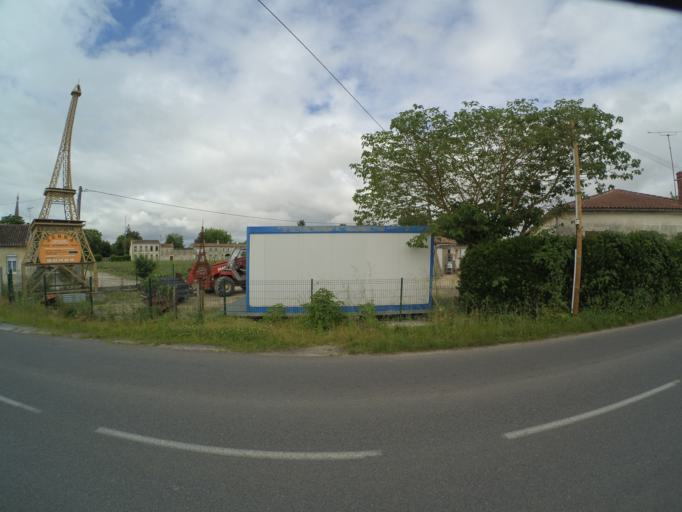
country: FR
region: Aquitaine
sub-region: Departement de la Gironde
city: Soussans
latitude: 45.0557
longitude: -0.6986
